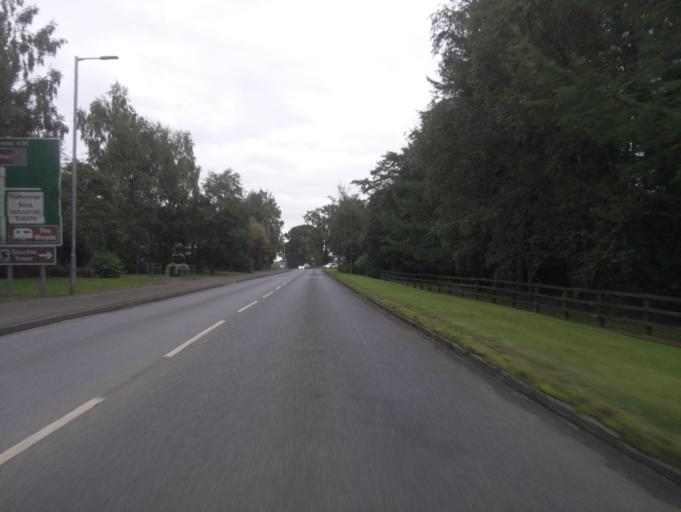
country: GB
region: Scotland
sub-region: Clackmannanshire
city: Alva
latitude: 56.1525
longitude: -3.7871
